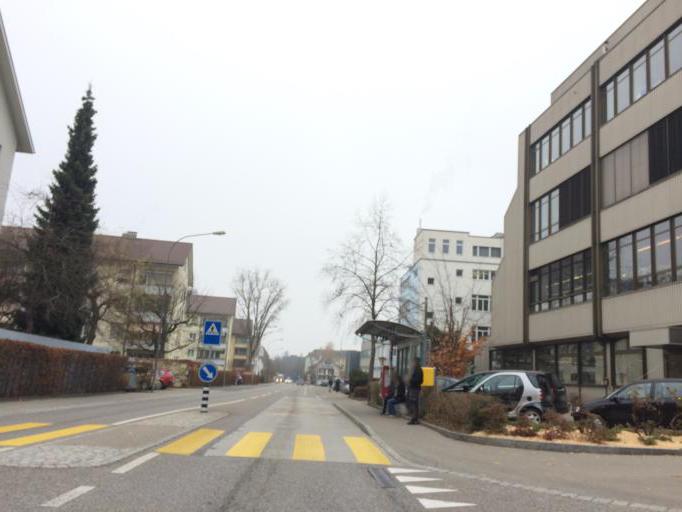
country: CH
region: Bern
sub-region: Bern-Mittelland District
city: Koniz
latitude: 46.9265
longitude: 7.4144
